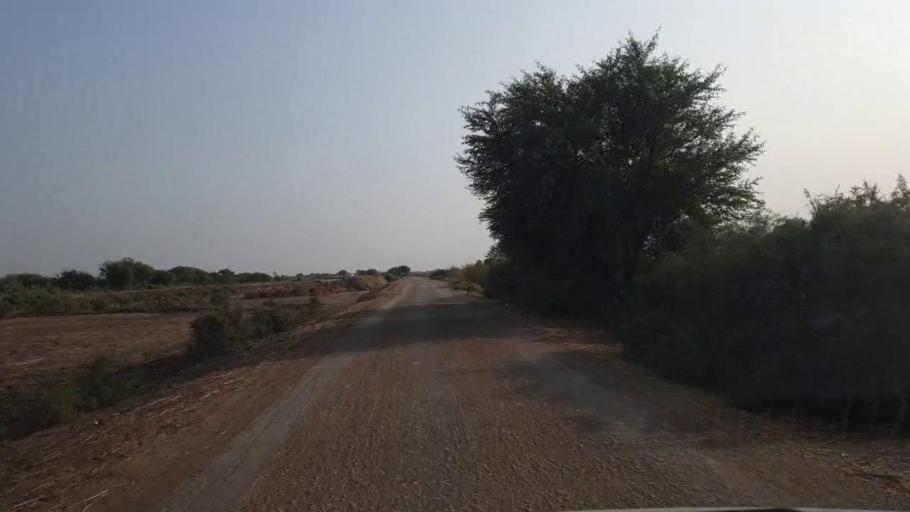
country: PK
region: Sindh
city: Matli
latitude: 25.0553
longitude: 68.7630
